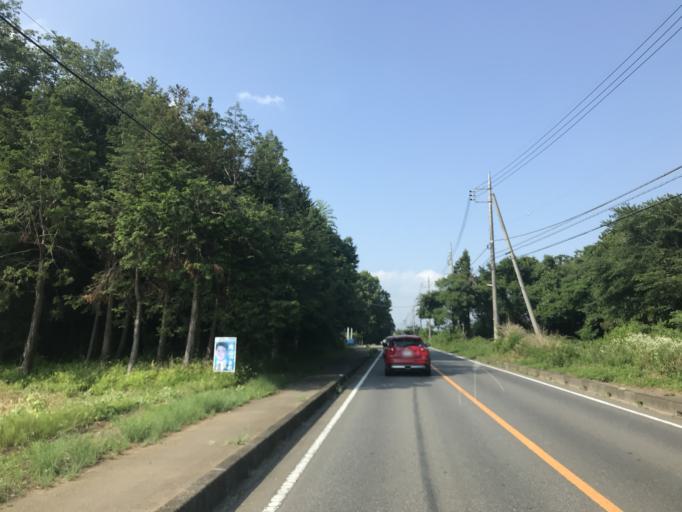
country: JP
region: Ibaraki
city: Naka
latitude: 36.0629
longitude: 140.0930
